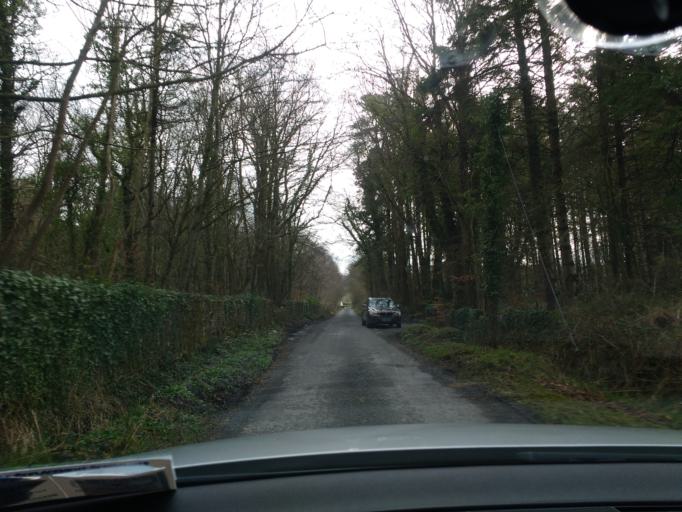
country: IE
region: Leinster
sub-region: Laois
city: Rathdowney
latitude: 52.6634
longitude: -7.5639
